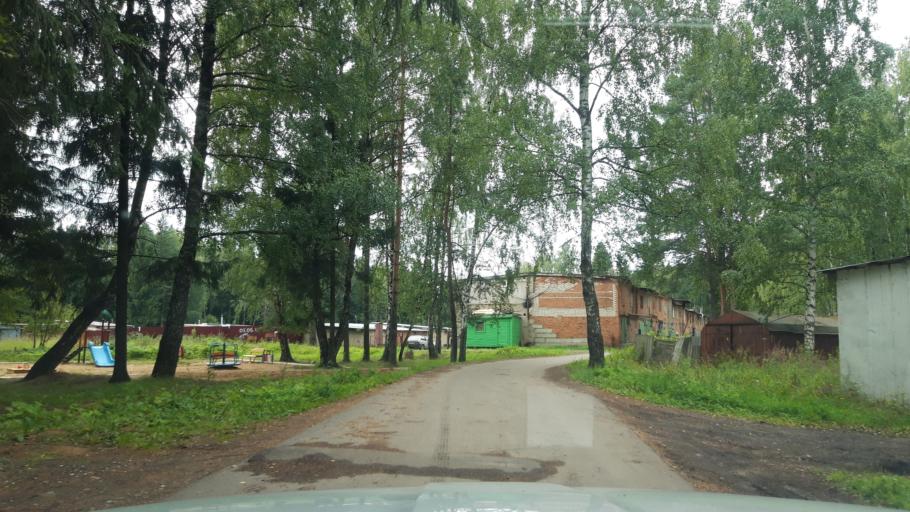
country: RU
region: Moskovskaya
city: Povarovo
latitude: 56.0607
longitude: 37.0779
